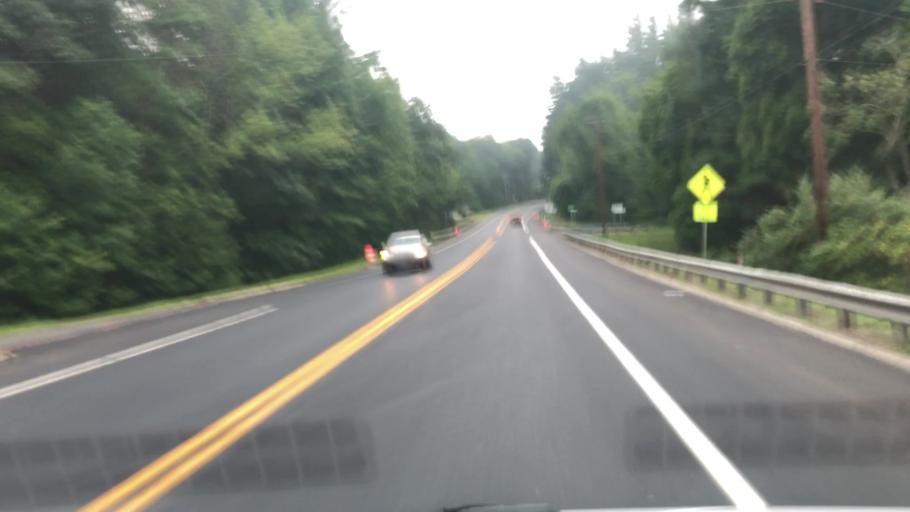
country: US
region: Massachusetts
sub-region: Franklin County
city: Shelburne Falls
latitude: 42.6143
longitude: -72.7390
